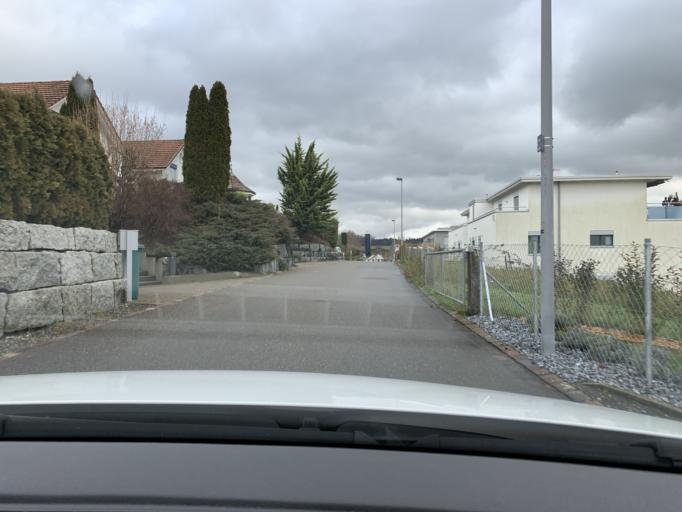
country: CH
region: Zurich
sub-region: Bezirk Dielsdorf
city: Sonnhalde
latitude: 47.4553
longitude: 8.4601
